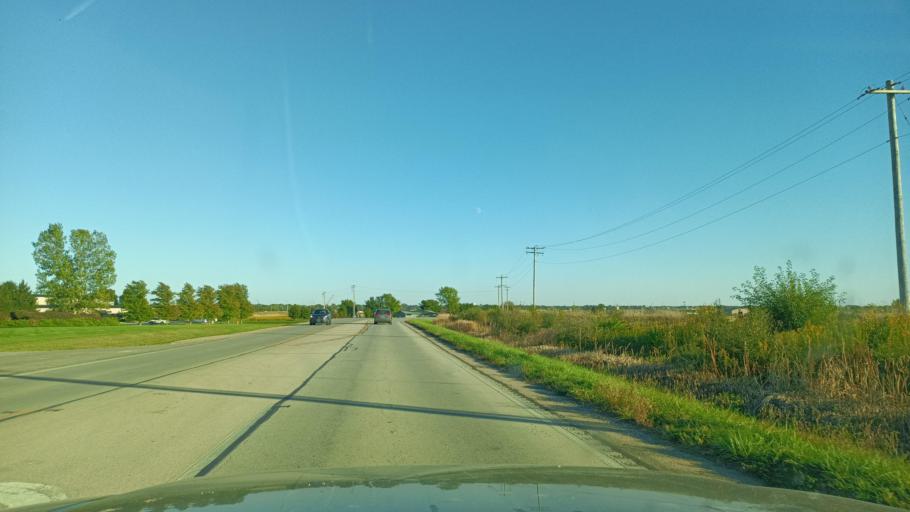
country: US
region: Illinois
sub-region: Champaign County
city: Champaign
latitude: 40.1501
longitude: -88.2939
